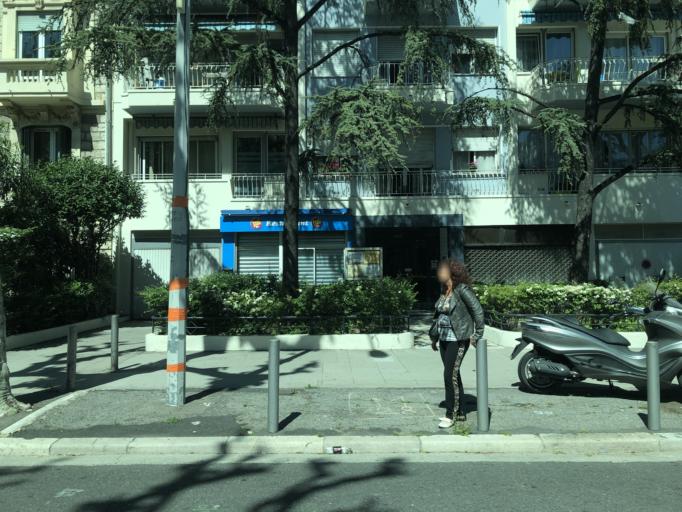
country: FR
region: Provence-Alpes-Cote d'Azur
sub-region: Departement des Alpes-Maritimes
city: Nice
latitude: 43.7057
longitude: 7.2837
